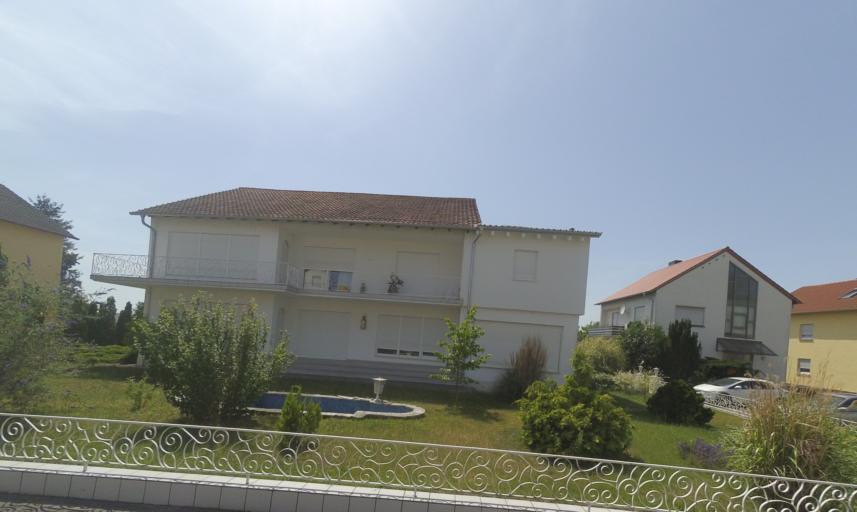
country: DE
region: Rheinland-Pfalz
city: Waldsee
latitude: 49.3935
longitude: 8.4330
